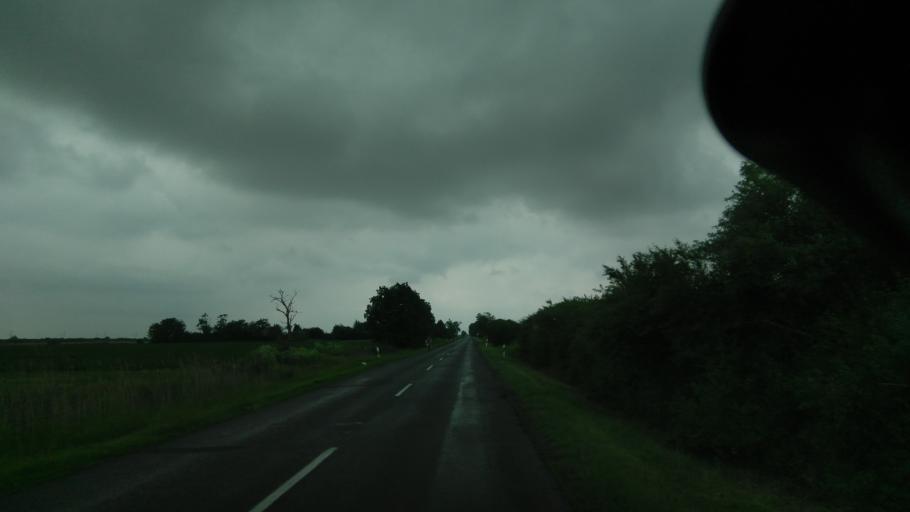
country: HU
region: Bekes
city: Szabadkigyos
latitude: 46.6284
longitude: 21.1045
